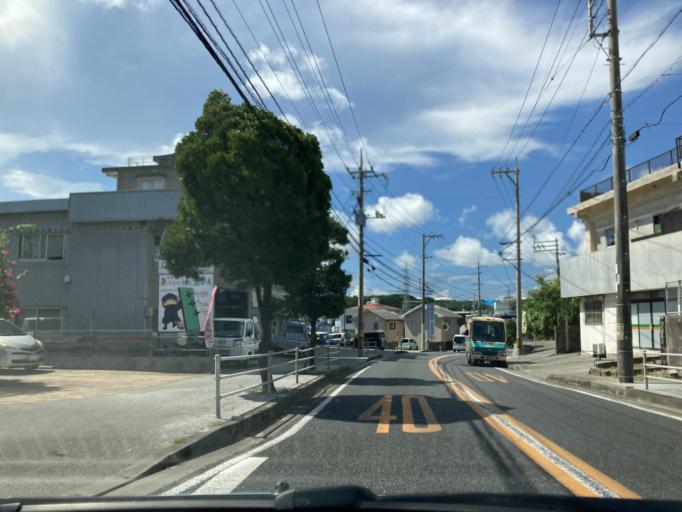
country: JP
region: Okinawa
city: Tomigusuku
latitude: 26.1702
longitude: 127.7216
